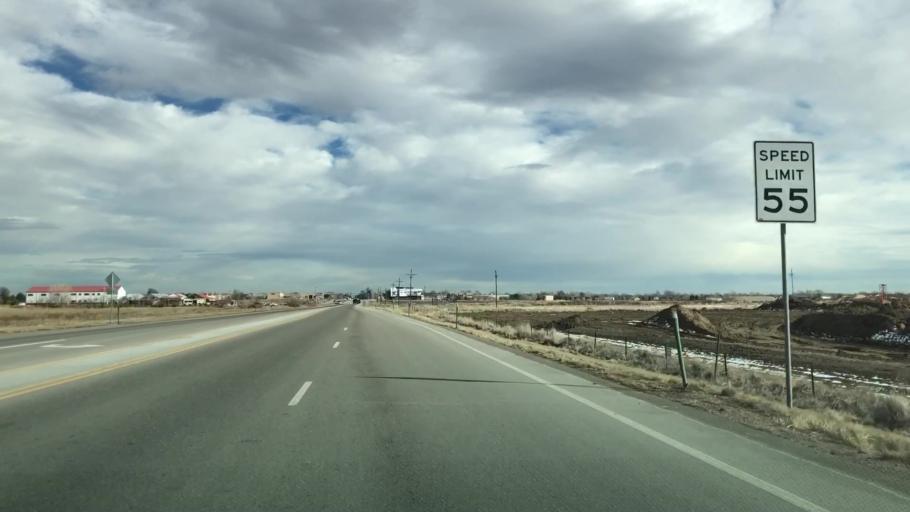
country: US
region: Colorado
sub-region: Weld County
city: Windsor
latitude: 40.4792
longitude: -104.9422
